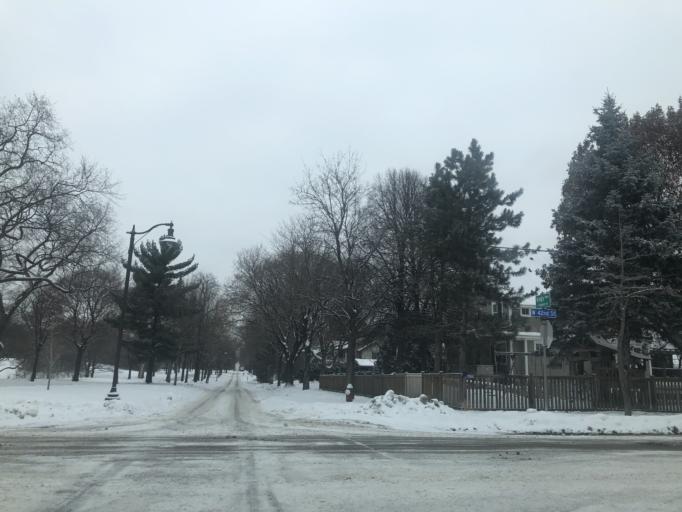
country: US
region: Minnesota
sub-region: Hennepin County
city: Richfield
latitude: 44.9268
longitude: -93.2934
